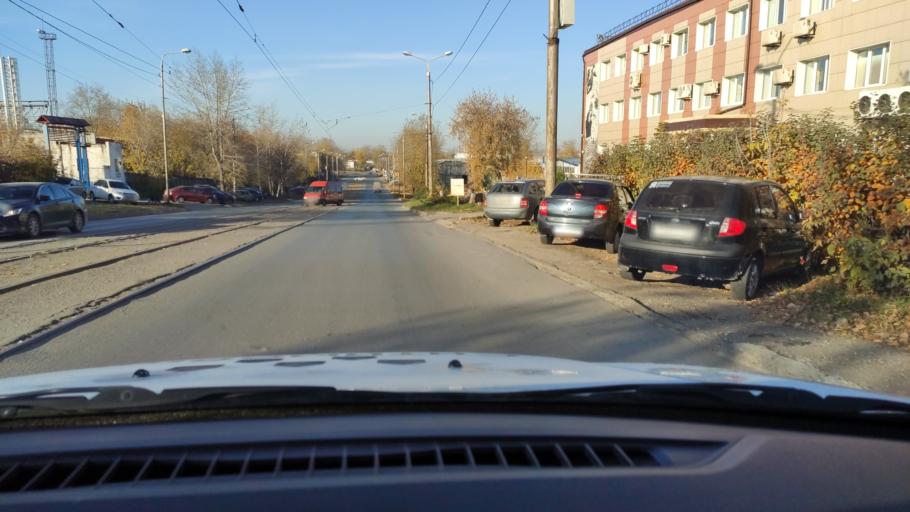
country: RU
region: Perm
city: Kondratovo
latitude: 58.0077
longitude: 56.1721
